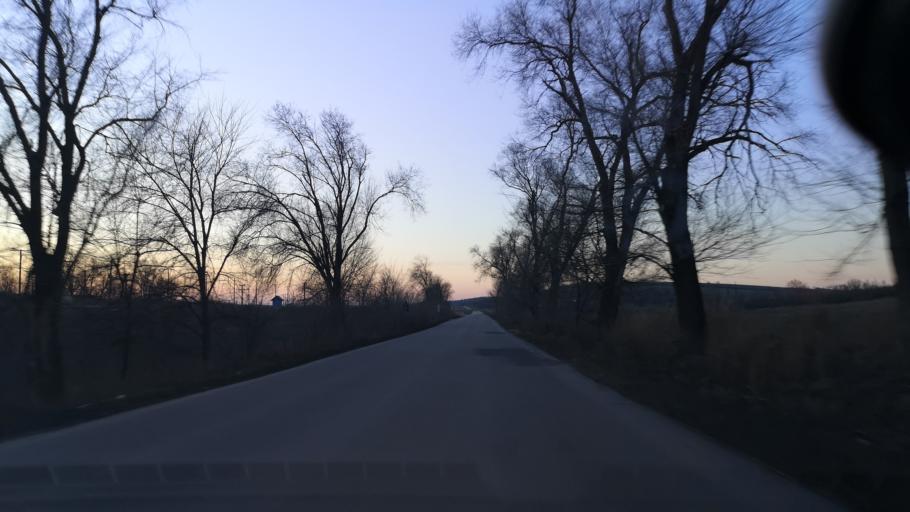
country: MD
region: Anenii Noi
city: Anenii Noi
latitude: 46.8902
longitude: 29.2451
